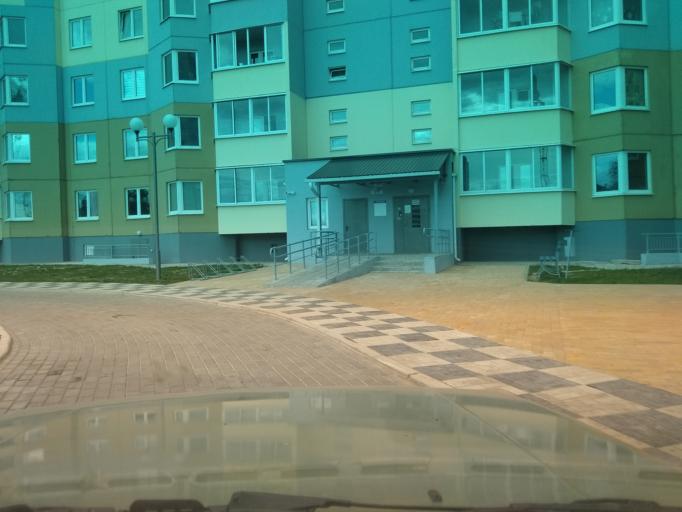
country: BY
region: Mogilev
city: Mahilyow
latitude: 53.9223
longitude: 30.3540
